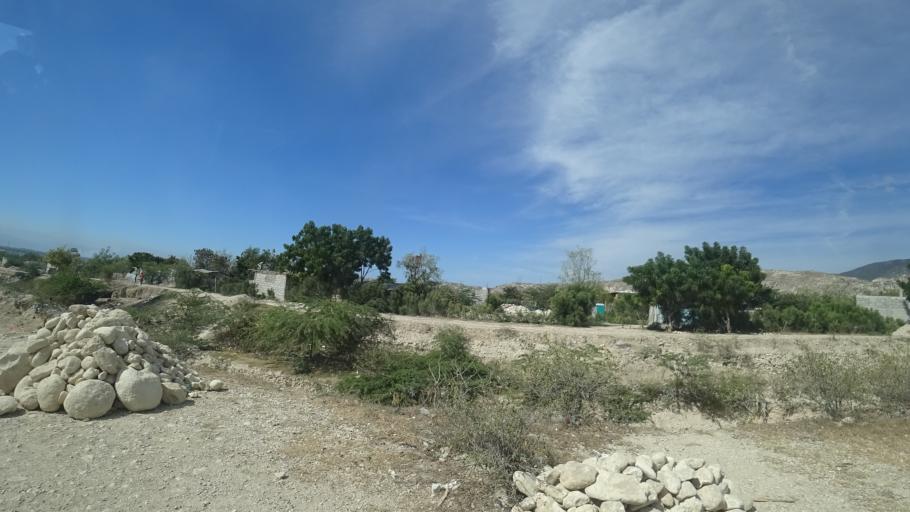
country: HT
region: Ouest
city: Croix des Bouquets
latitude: 18.6589
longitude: -72.2478
